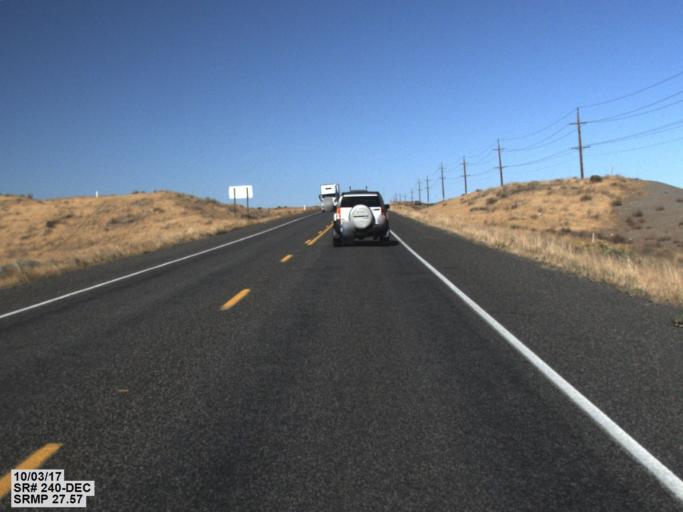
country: US
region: Washington
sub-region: Benton County
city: Richland
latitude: 46.3201
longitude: -119.3056
